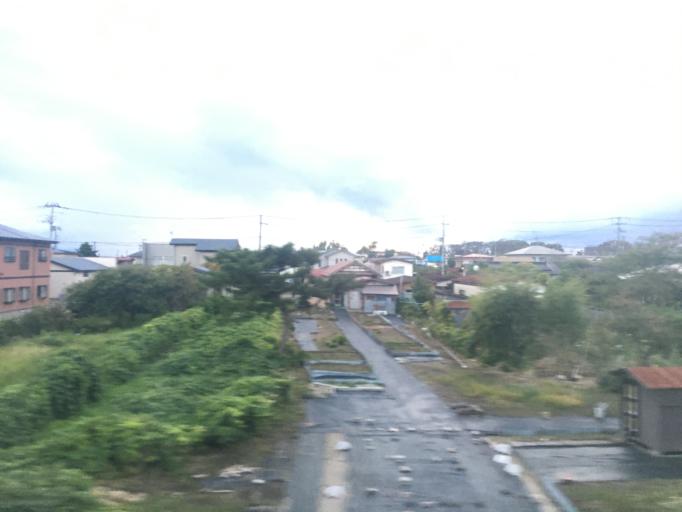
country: JP
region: Akita
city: Tenno
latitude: 39.9034
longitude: 139.9556
